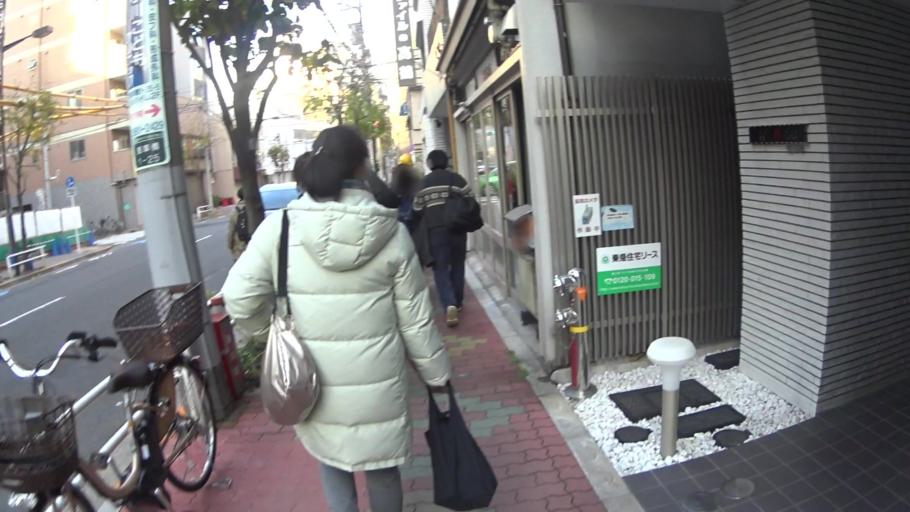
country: JP
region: Tokyo
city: Tokyo
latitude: 35.6984
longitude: 139.7829
